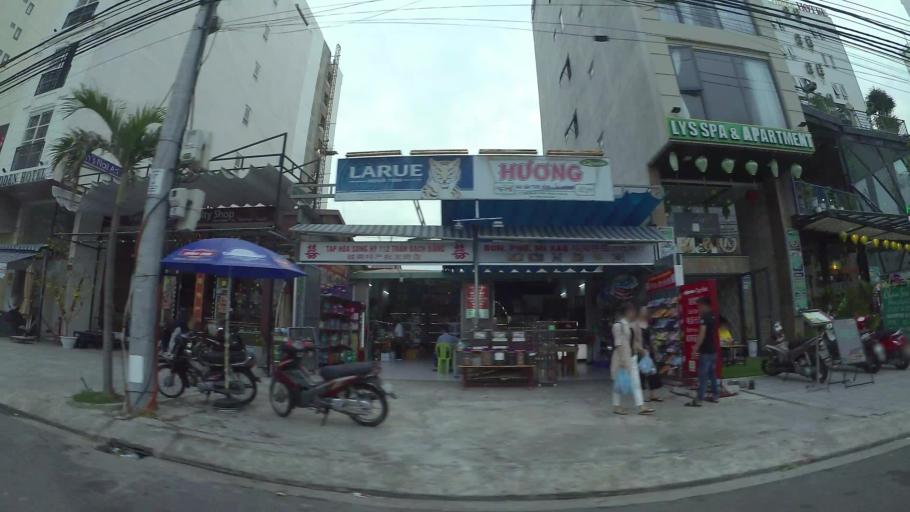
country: VN
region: Da Nang
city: Son Tra
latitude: 16.0547
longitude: 108.2460
